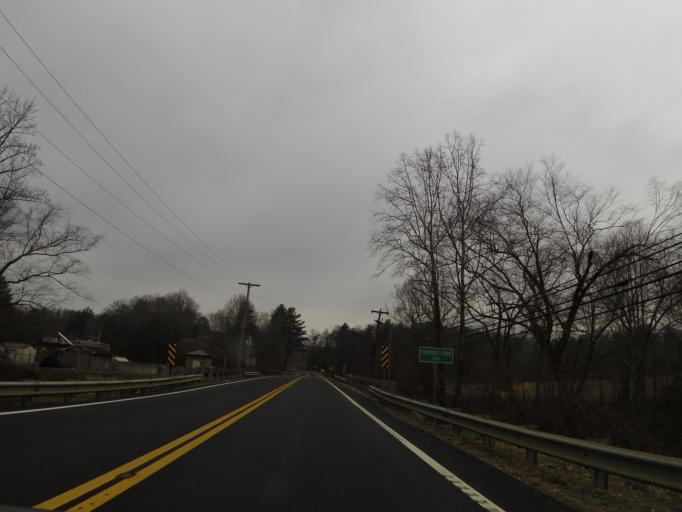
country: US
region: Tennessee
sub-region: Morgan County
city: Wartburg
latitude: 36.0847
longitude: -84.5546
